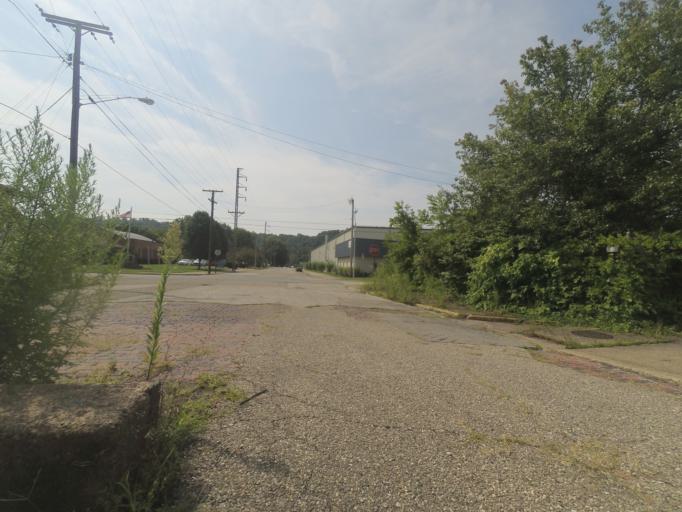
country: US
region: West Virginia
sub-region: Cabell County
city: Huntington
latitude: 38.4112
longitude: -82.4619
